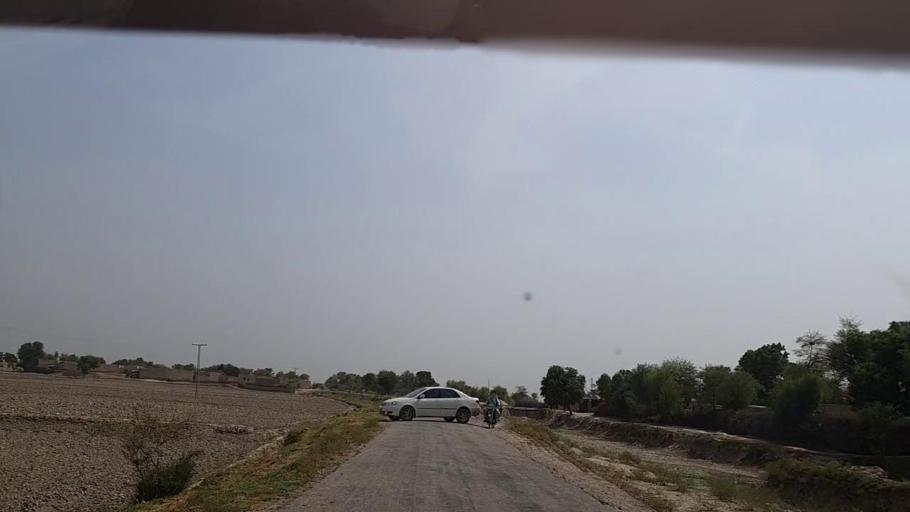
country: PK
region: Sindh
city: Khairpur Nathan Shah
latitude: 27.0681
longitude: 67.6878
